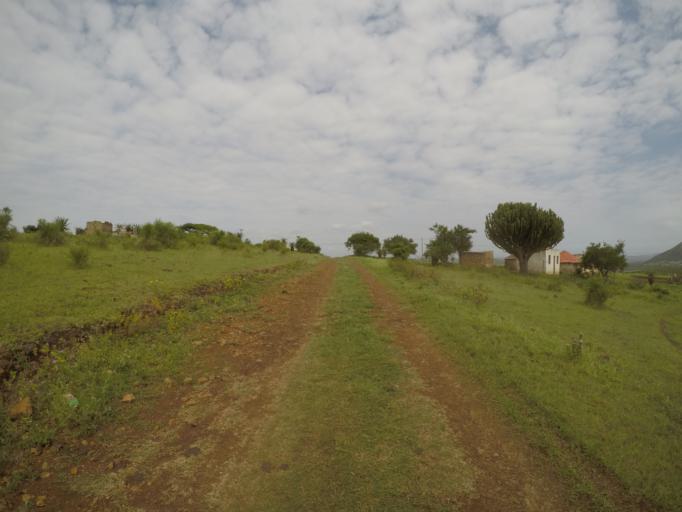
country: ZA
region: KwaZulu-Natal
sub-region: uThungulu District Municipality
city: Empangeni
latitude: -28.6161
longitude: 31.8964
